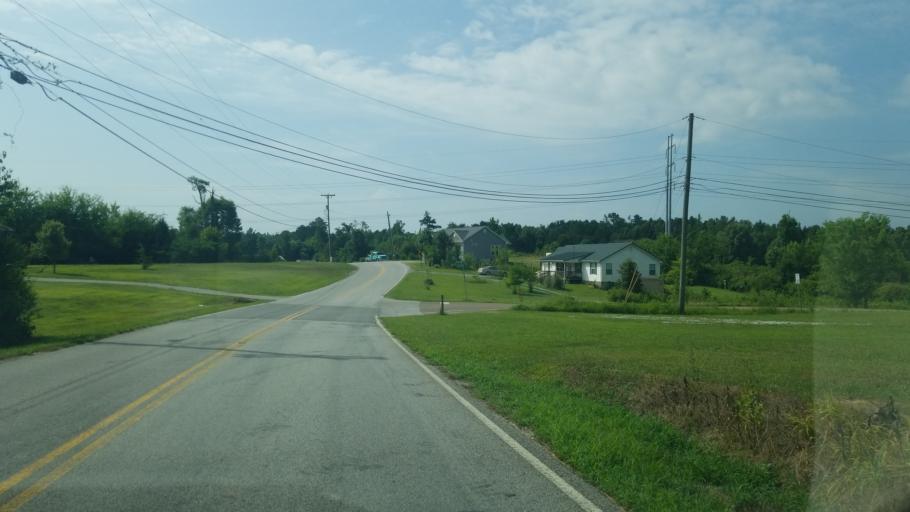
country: US
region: Tennessee
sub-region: Hamilton County
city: Apison
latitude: 35.0170
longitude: -85.0112
